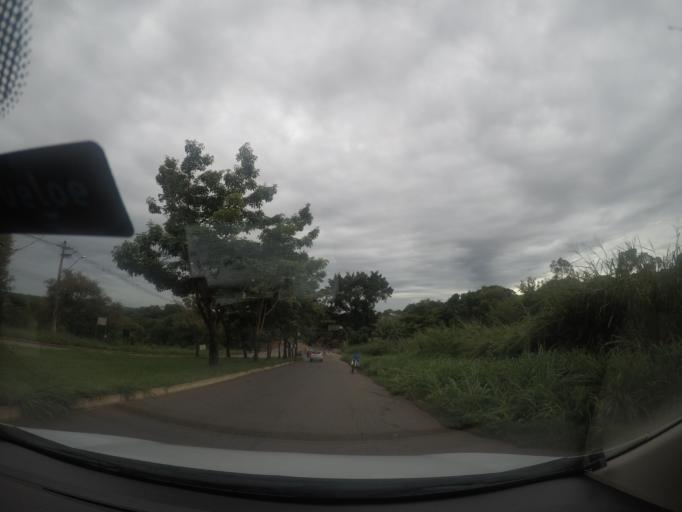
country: BR
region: Goias
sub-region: Goiania
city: Goiania
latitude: -16.6055
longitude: -49.2991
